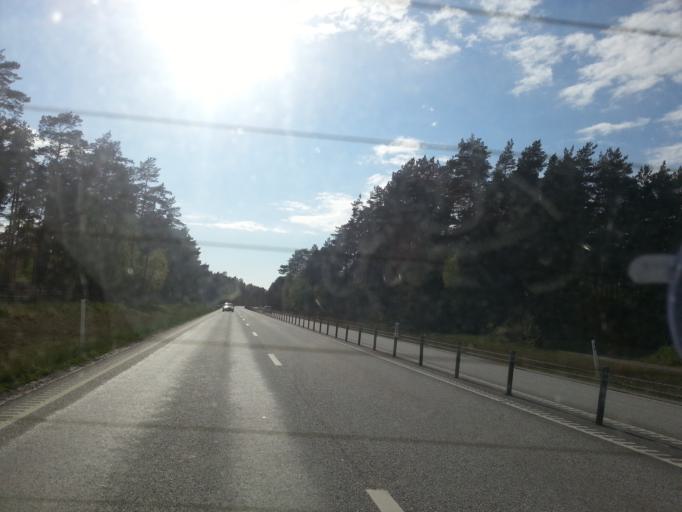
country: SE
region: Skane
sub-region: Lunds Kommun
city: Veberod
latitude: 55.6407
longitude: 13.5240
